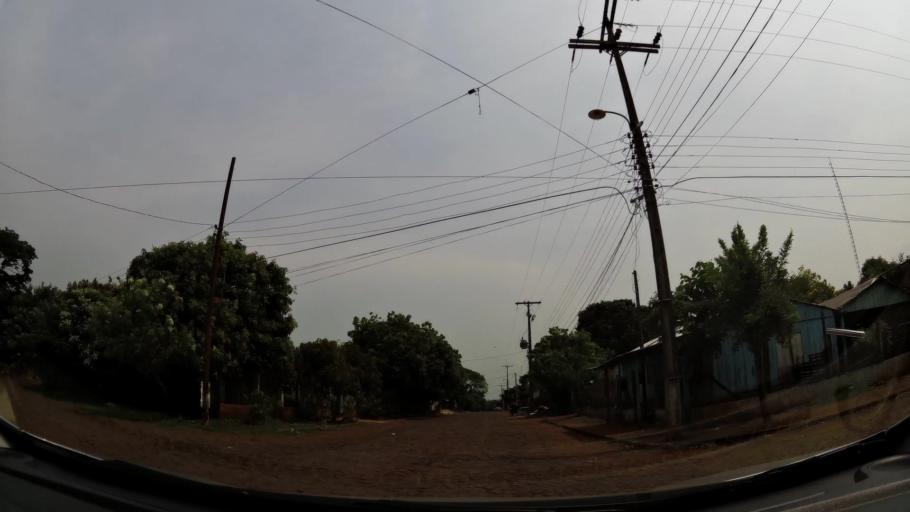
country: BR
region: Parana
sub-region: Foz Do Iguacu
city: Foz do Iguacu
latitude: -25.5703
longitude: -54.6101
